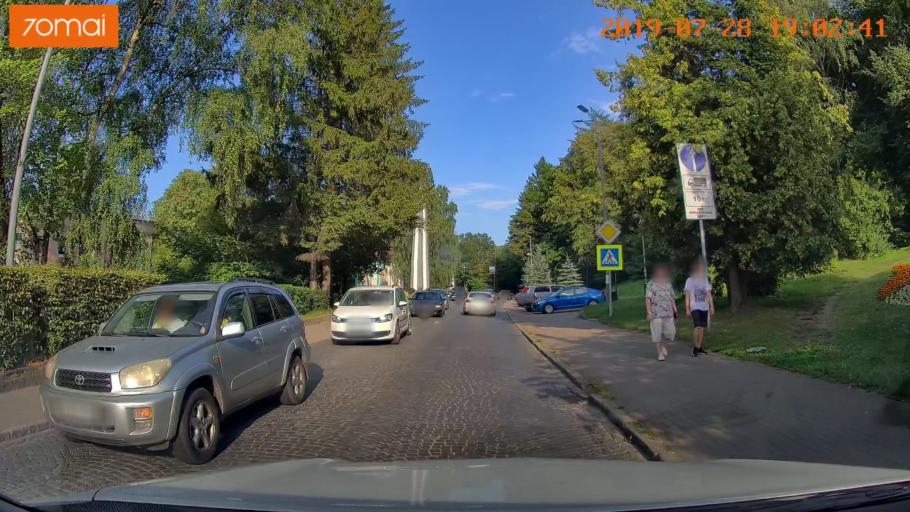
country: RU
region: Kaliningrad
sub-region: Gorod Svetlogorsk
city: Svetlogorsk
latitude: 54.9381
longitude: 20.1612
